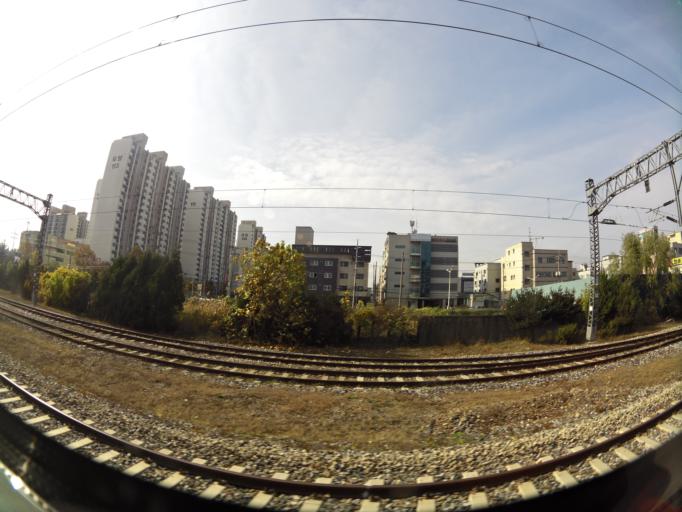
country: KR
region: Daejeon
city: Songgang-dong
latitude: 36.6040
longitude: 127.2950
